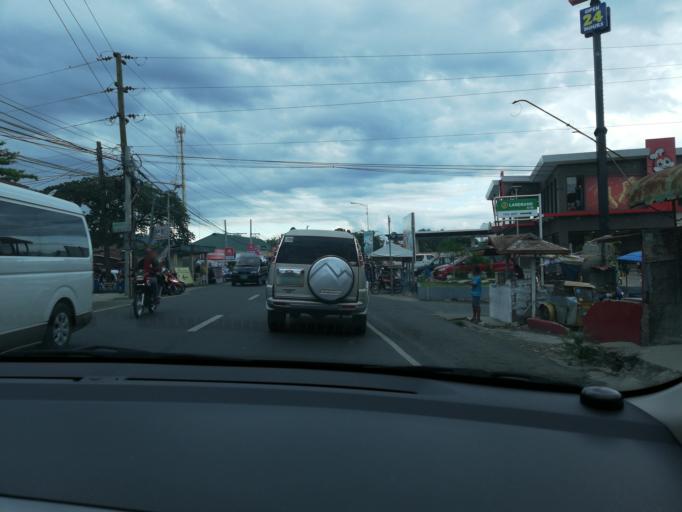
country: PH
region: Ilocos
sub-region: Province of Ilocos Sur
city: Narvacan
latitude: 17.4186
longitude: 120.4739
